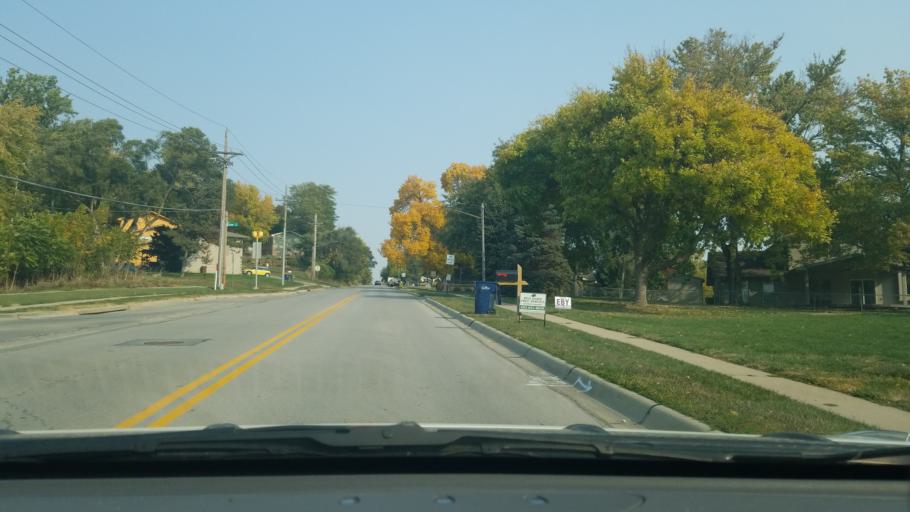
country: US
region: Nebraska
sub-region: Sarpy County
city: Bellevue
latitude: 41.1547
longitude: -95.9090
